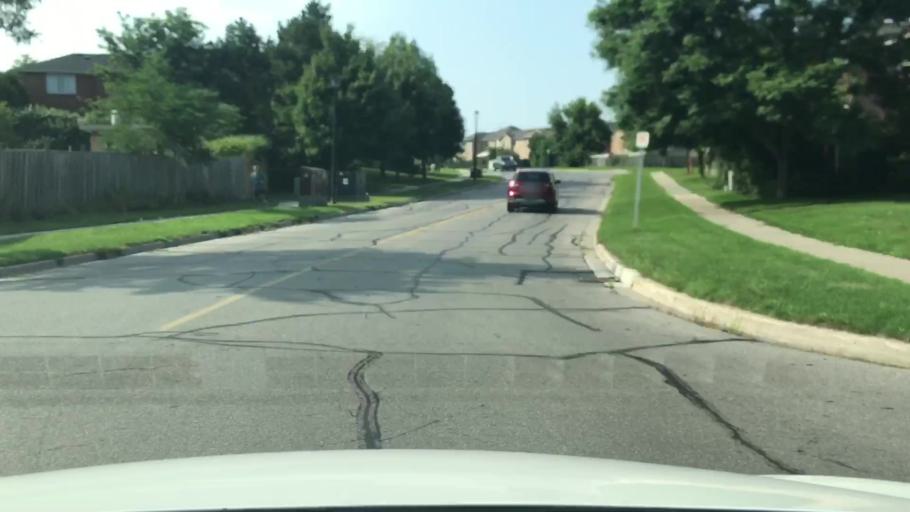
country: CA
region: Ontario
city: Newmarket
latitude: 44.0448
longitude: -79.4470
